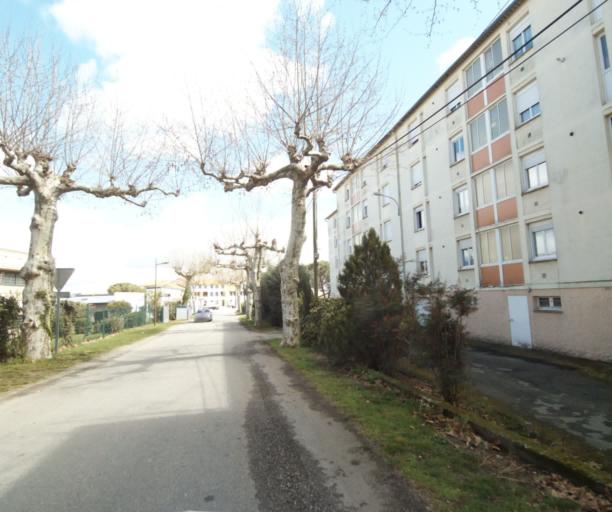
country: FR
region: Midi-Pyrenees
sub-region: Departement de l'Ariege
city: Saverdun
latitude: 43.2394
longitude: 1.5736
